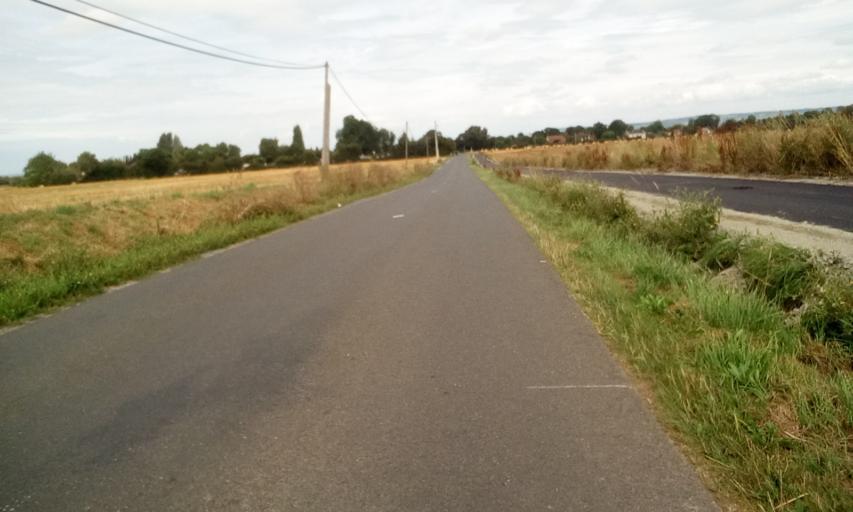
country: FR
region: Lower Normandy
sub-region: Departement du Calvados
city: Amfreville
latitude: 49.2441
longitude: -0.2172
